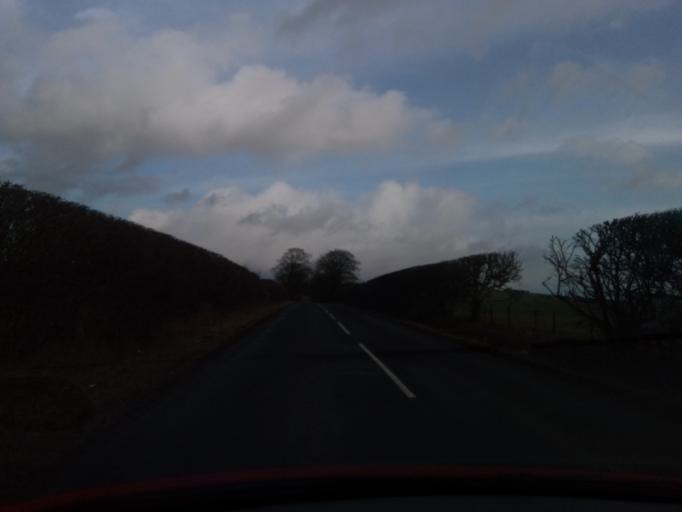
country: GB
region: England
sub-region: Northumberland
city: Rothley
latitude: 55.1235
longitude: -2.0049
